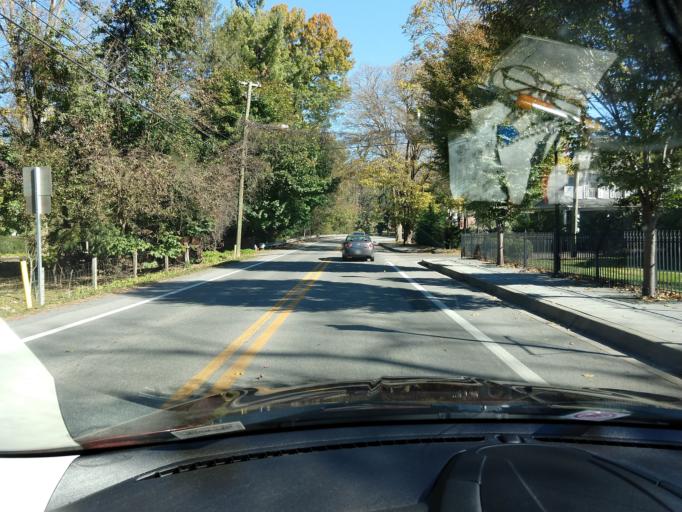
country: US
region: West Virginia
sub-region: Greenbrier County
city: Lewisburg
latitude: 37.8051
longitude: -80.4406
